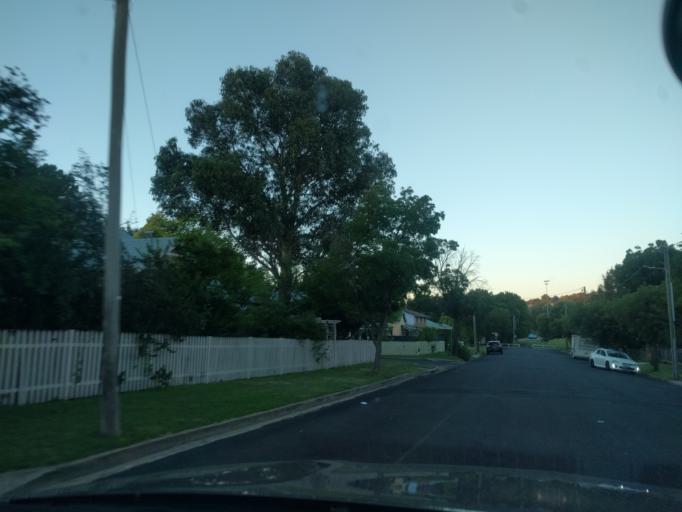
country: AU
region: New South Wales
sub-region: Armidale Dumaresq
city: Armidale
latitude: -30.5104
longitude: 151.6571
